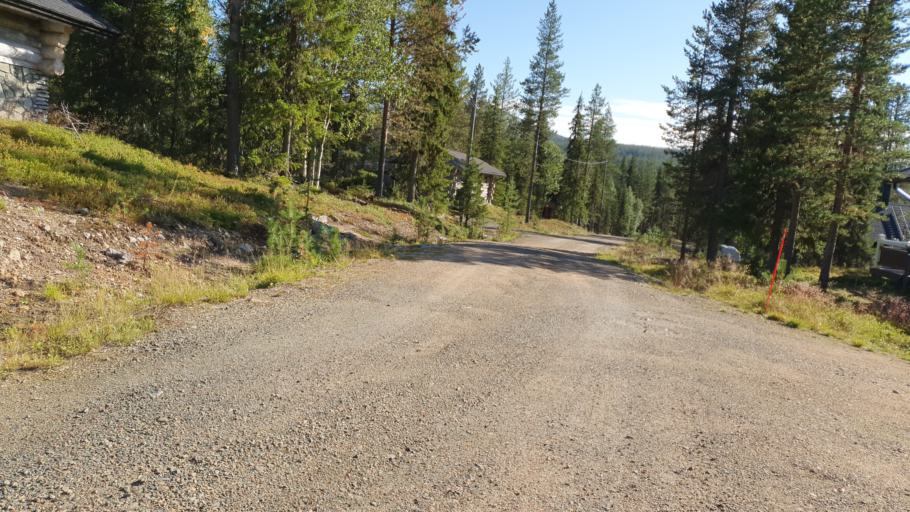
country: FI
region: Lapland
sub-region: Tunturi-Lappi
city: Kolari
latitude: 67.6069
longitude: 24.2068
